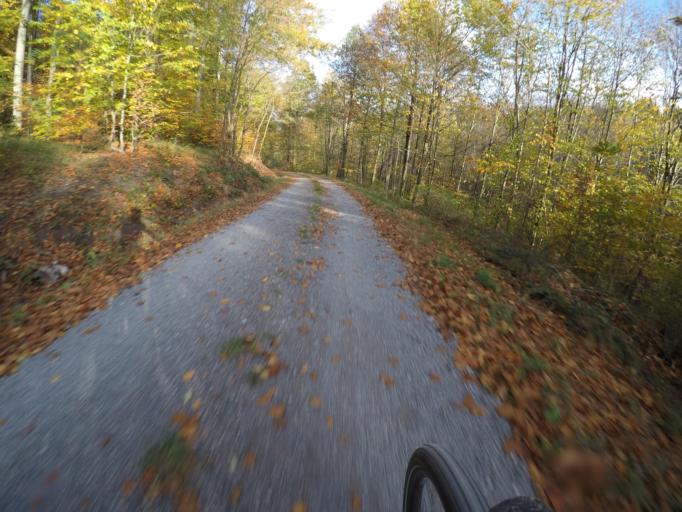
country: DE
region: Baden-Wuerttemberg
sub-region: Regierungsbezirk Stuttgart
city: Steinenbronn
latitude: 48.7003
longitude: 9.0844
